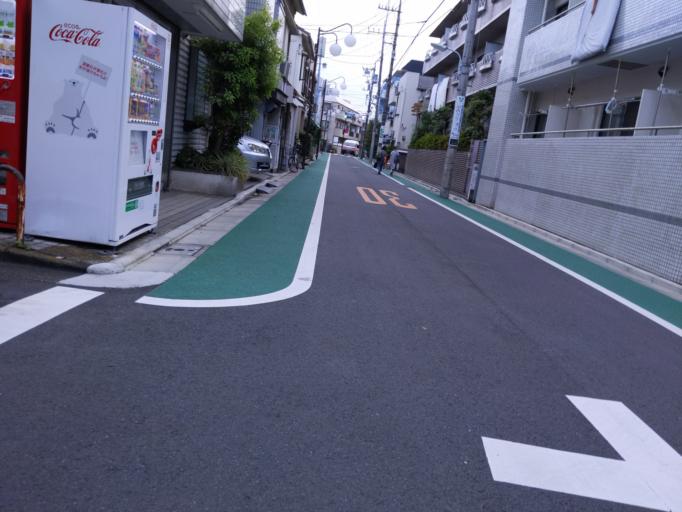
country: JP
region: Tokyo
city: Tokyo
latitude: 35.6169
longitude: 139.7017
